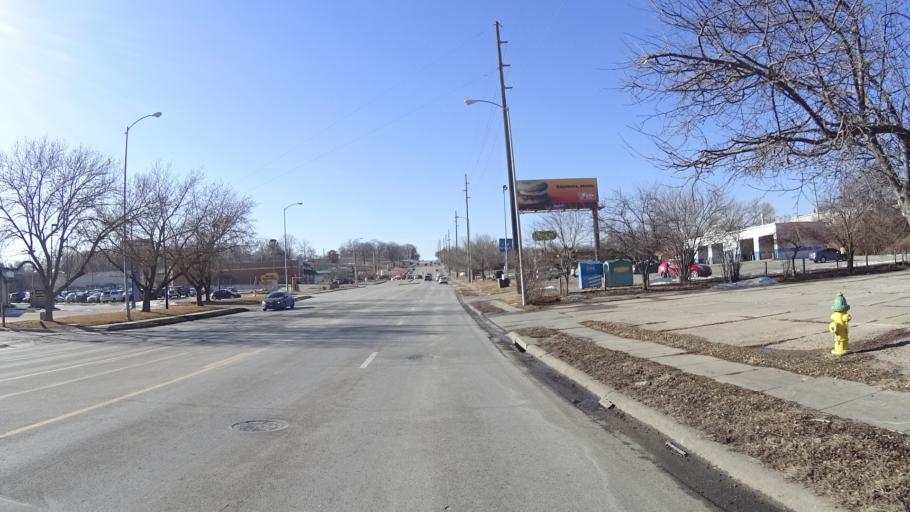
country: US
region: Nebraska
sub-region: Douglas County
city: Ralston
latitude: 41.3068
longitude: -96.0498
